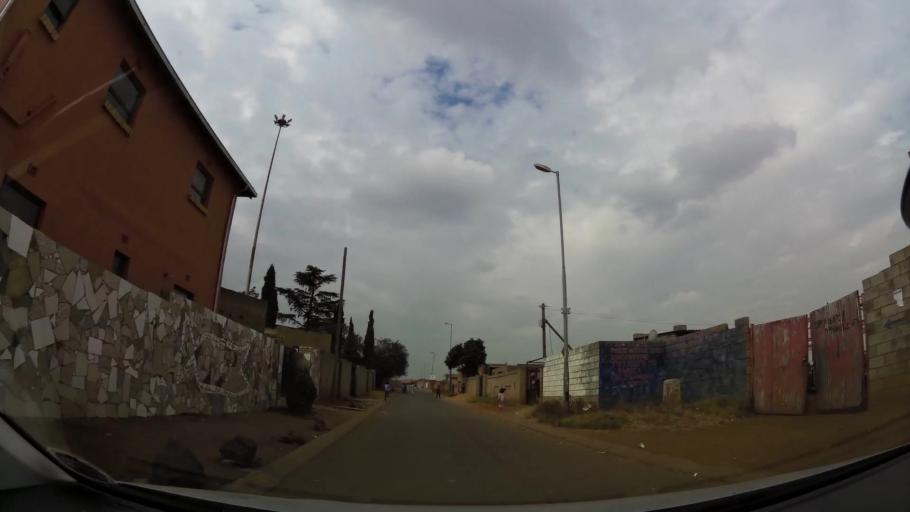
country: ZA
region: Gauteng
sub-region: City of Johannesburg Metropolitan Municipality
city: Soweto
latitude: -26.2626
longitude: 27.8521
